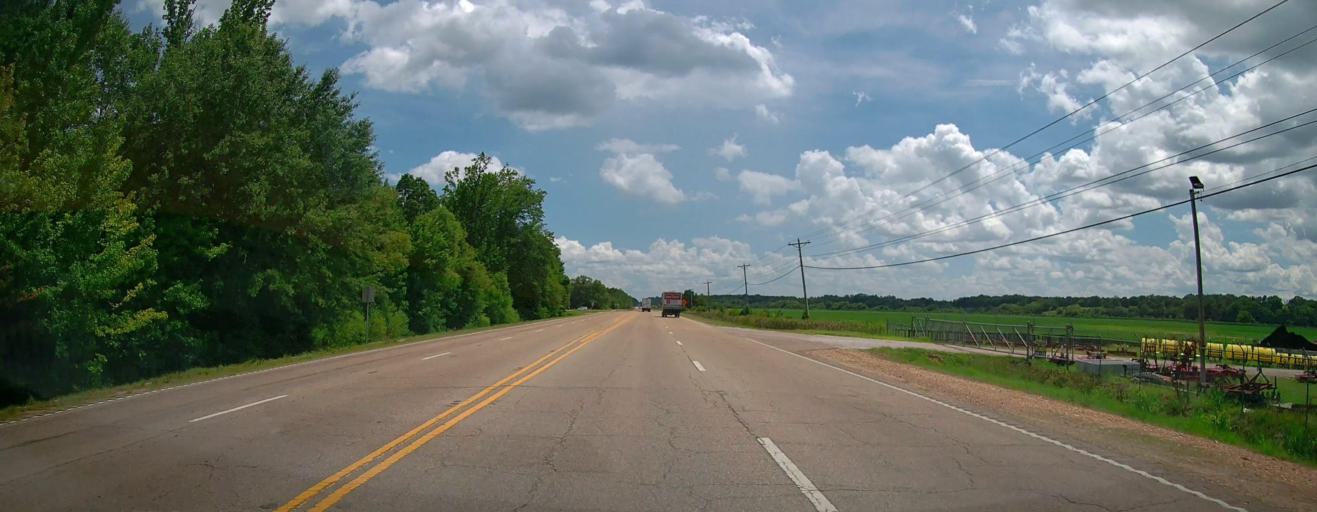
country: US
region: Mississippi
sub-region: Lee County
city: Verona
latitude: 34.1552
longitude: -88.7195
